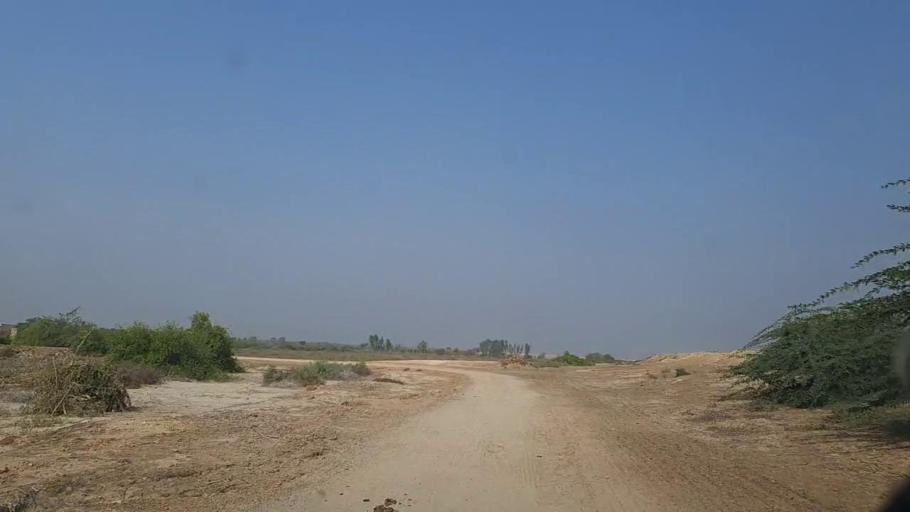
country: PK
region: Sindh
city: Thatta
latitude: 24.6642
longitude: 67.9252
